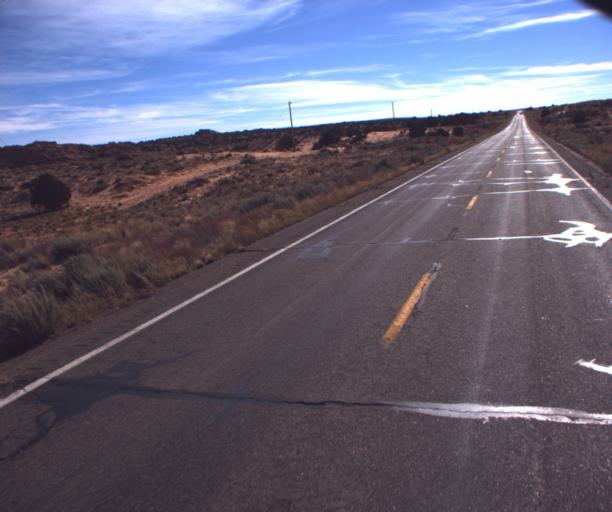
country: US
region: Arizona
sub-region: Coconino County
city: Kaibito
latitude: 36.6055
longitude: -111.1776
